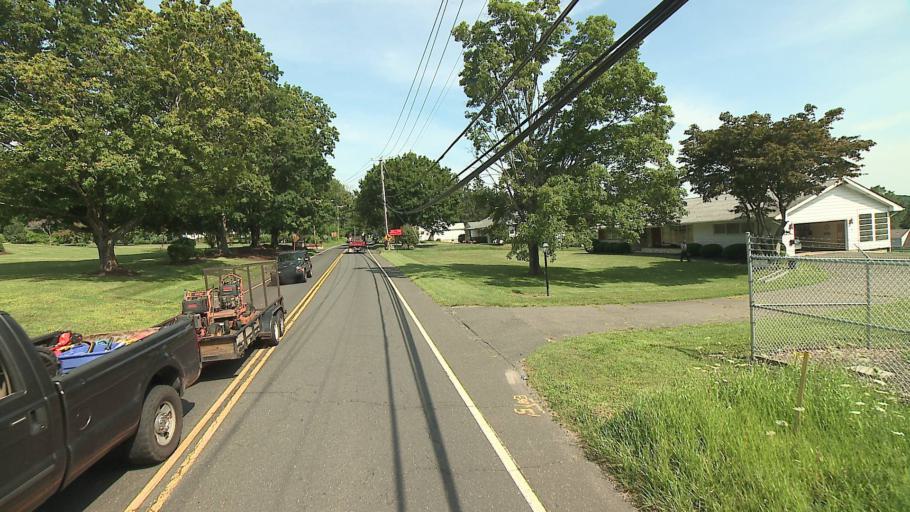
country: US
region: Connecticut
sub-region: Fairfield County
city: Danbury
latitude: 41.4116
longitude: -73.4697
